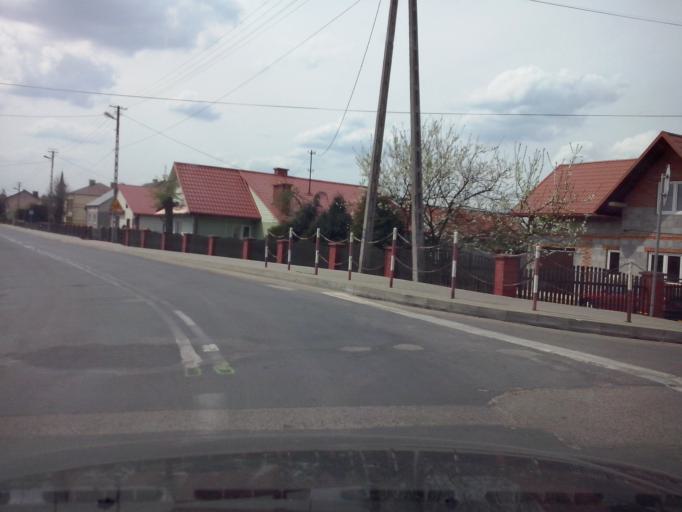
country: PL
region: Subcarpathian Voivodeship
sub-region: Powiat lezajski
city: Letownia
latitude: 50.3688
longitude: 22.2176
